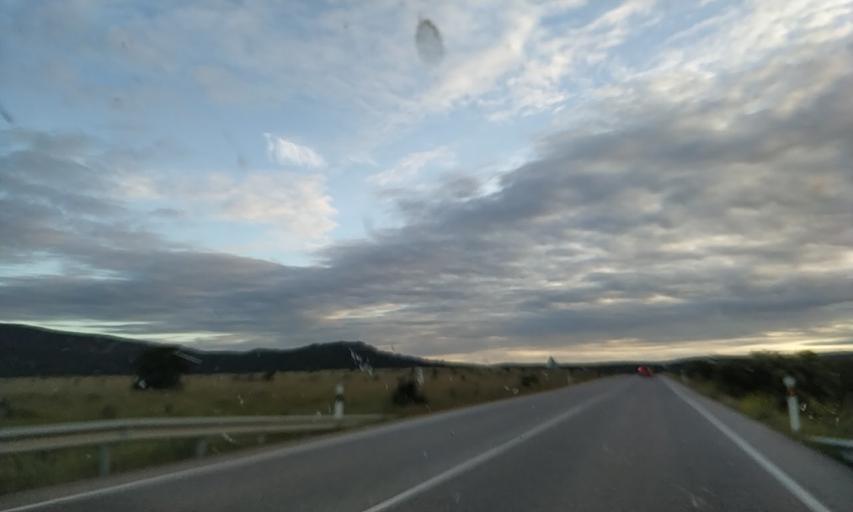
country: ES
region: Extremadura
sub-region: Provincia de Caceres
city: Malpartida de Caceres
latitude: 39.3212
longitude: -6.4998
